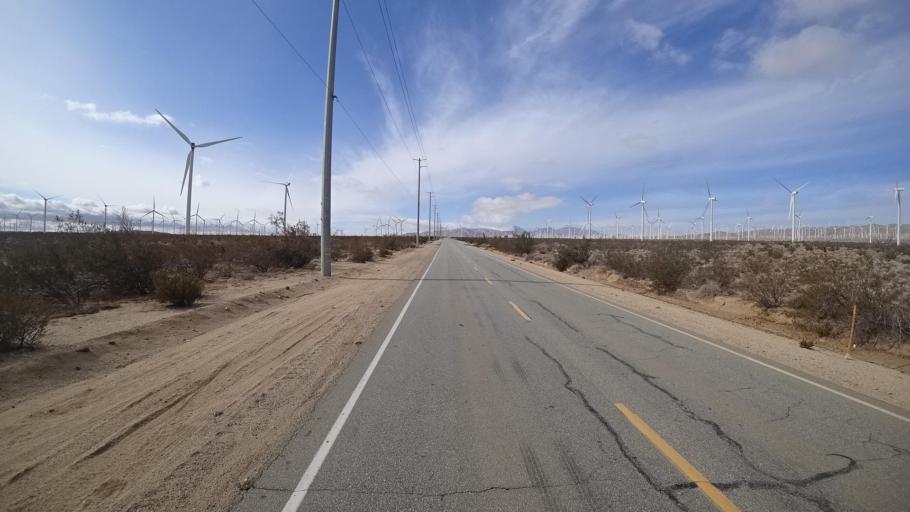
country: US
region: California
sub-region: Kern County
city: Mojave
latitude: 35.0434
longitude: -118.2282
